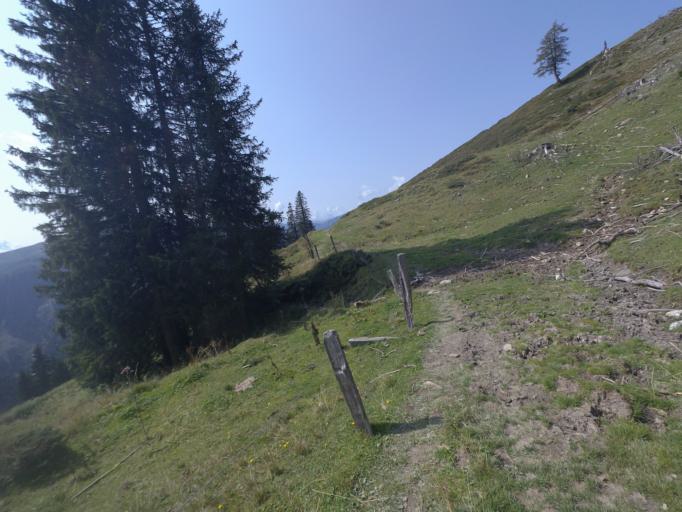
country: AT
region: Salzburg
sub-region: Politischer Bezirk Sankt Johann im Pongau
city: Kleinarl
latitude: 47.2771
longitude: 13.2661
